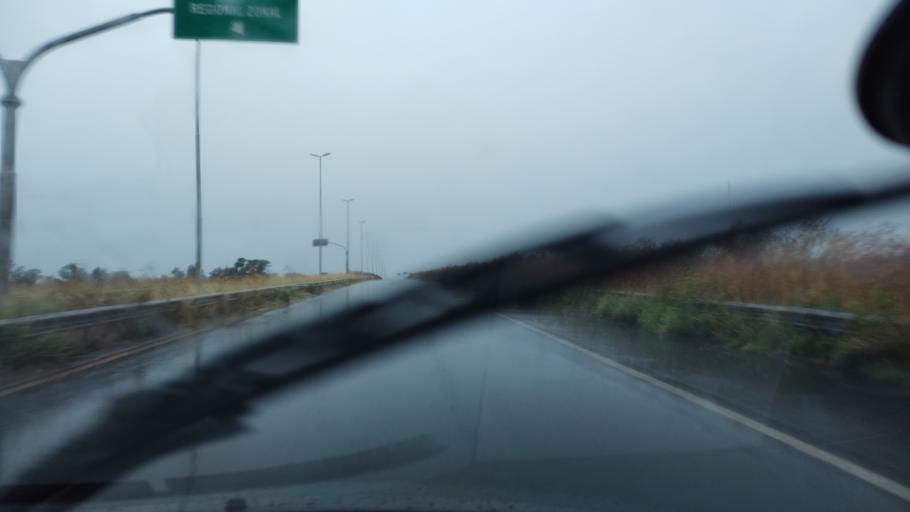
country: AR
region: Buenos Aires
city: Canuelas
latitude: -35.0262
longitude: -58.7340
